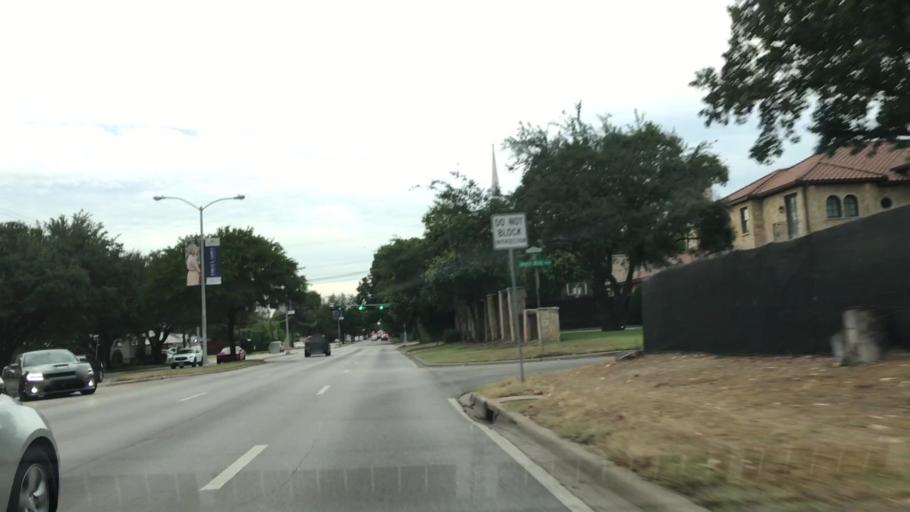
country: US
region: Texas
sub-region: Dallas County
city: University Park
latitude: 32.8790
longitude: -96.8039
